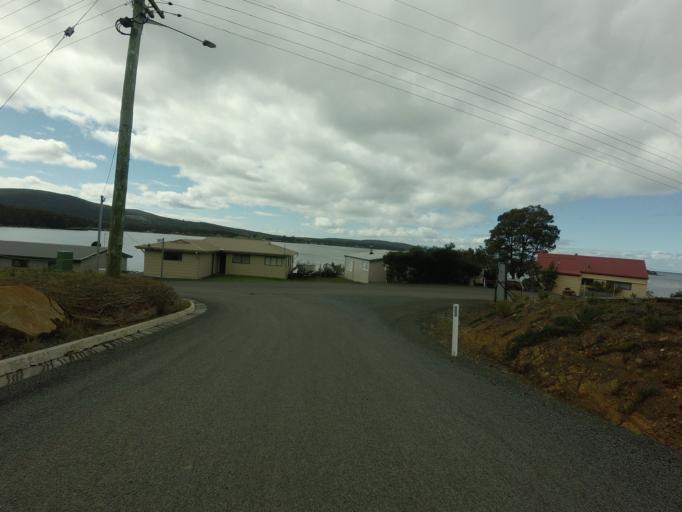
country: AU
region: Tasmania
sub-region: Huon Valley
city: Geeveston
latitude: -43.4439
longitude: 146.9611
